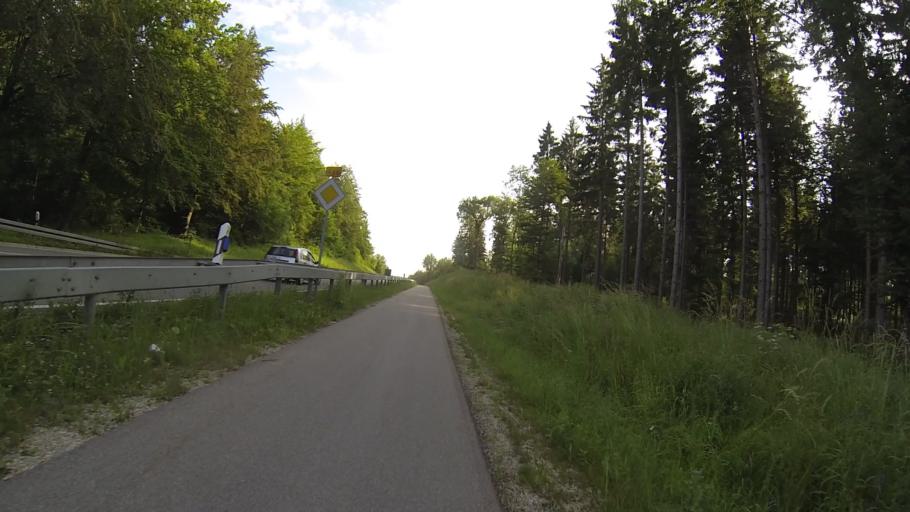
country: DE
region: Baden-Wuerttemberg
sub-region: Regierungsbezirk Stuttgart
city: Nattheim
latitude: 48.7211
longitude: 10.2522
